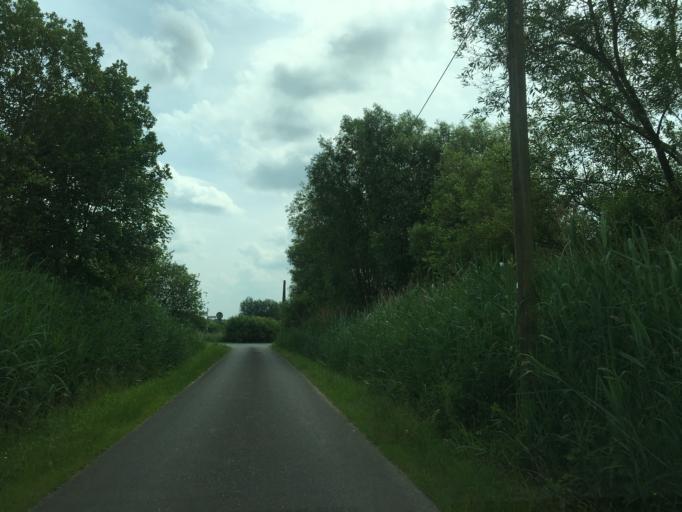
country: DE
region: North Rhine-Westphalia
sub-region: Regierungsbezirk Munster
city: Muenster
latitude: 52.0227
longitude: 7.6472
